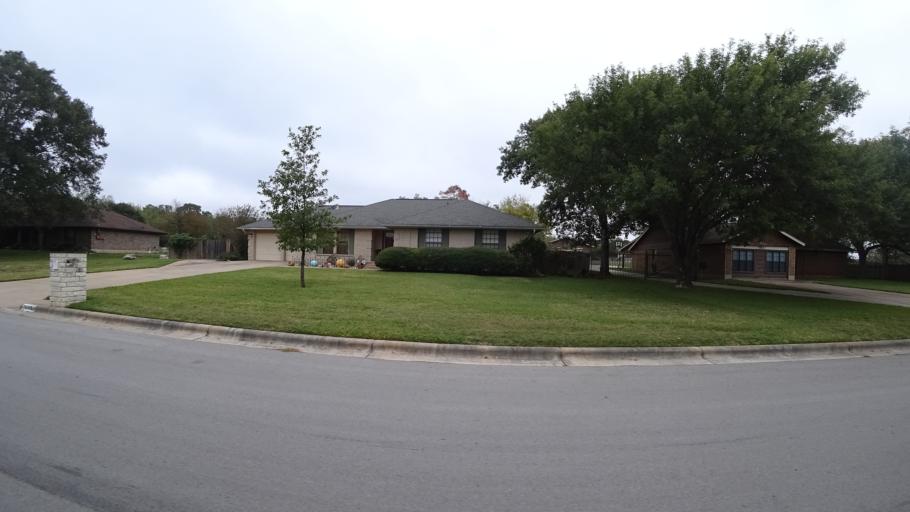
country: US
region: Texas
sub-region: Travis County
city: Shady Hollow
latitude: 30.2150
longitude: -97.9089
